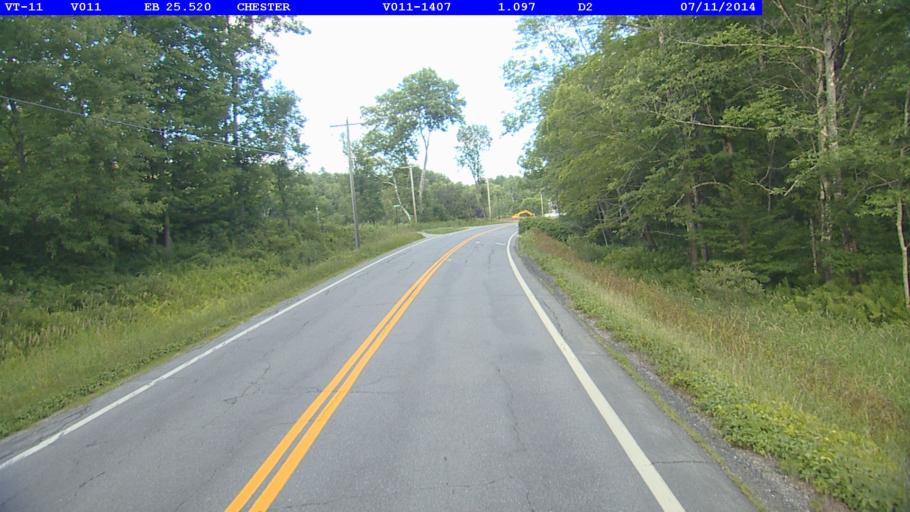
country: US
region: Vermont
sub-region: Windsor County
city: Chester
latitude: 43.2625
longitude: -72.6643
